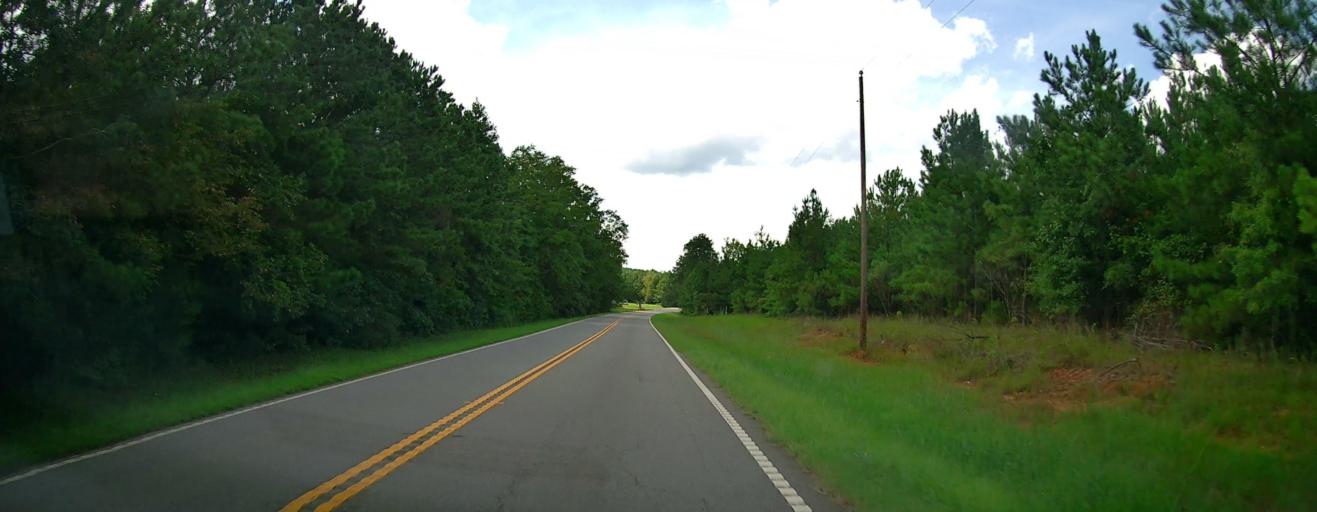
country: US
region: Georgia
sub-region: Talbot County
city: Talbotton
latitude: 32.6412
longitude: -84.4964
